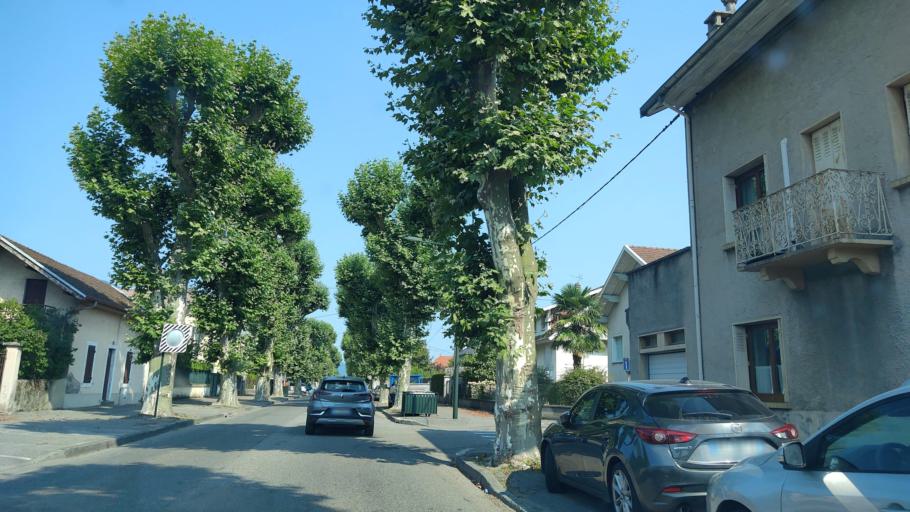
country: FR
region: Rhone-Alpes
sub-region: Departement de la Savoie
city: Tresserve
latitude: 45.7014
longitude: 5.9018
